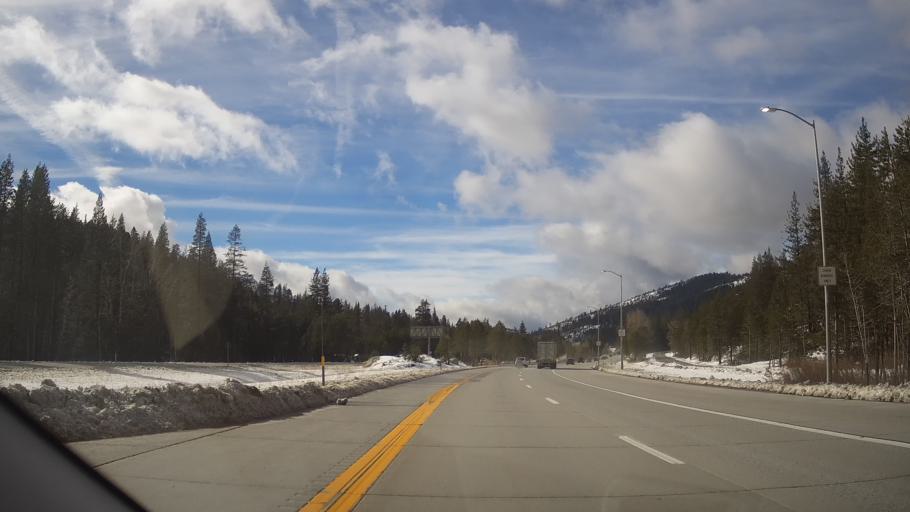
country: US
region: California
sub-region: Nevada County
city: Truckee
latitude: 39.3121
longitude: -120.4888
